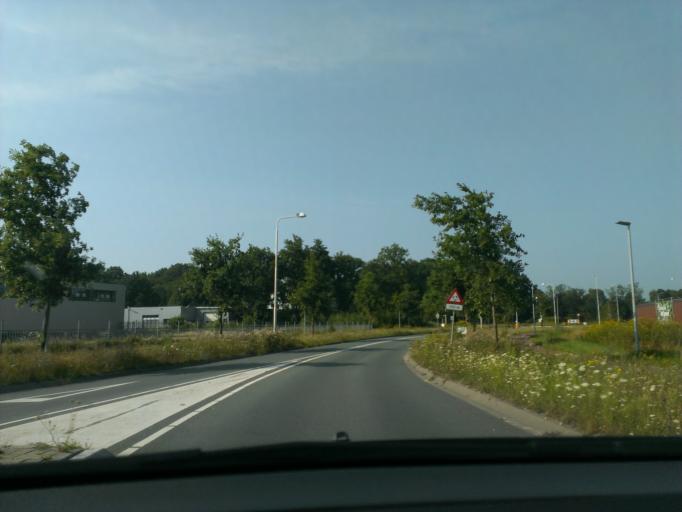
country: NL
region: Gelderland
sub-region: Gemeente Epe
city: Epe
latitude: 52.3445
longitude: 6.0010
